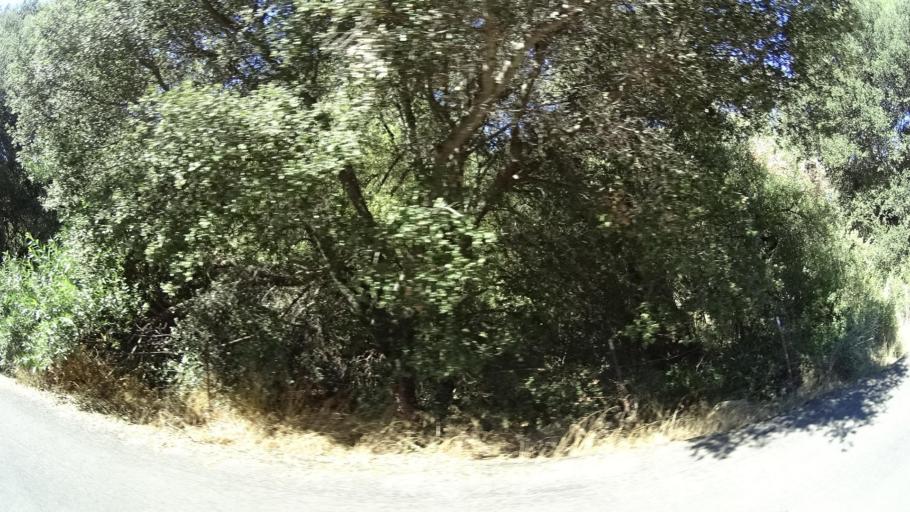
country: US
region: California
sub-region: San Diego County
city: Descanso
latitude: 32.8647
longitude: -116.6225
